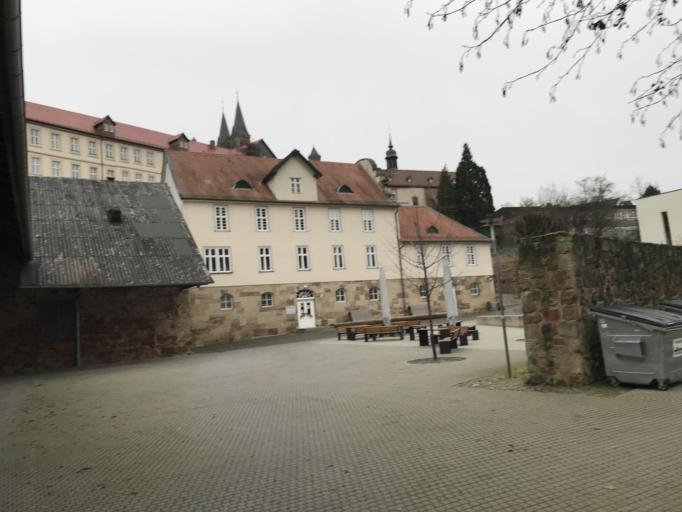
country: DE
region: Hesse
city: Fritzlar
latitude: 51.1287
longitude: 9.2723
